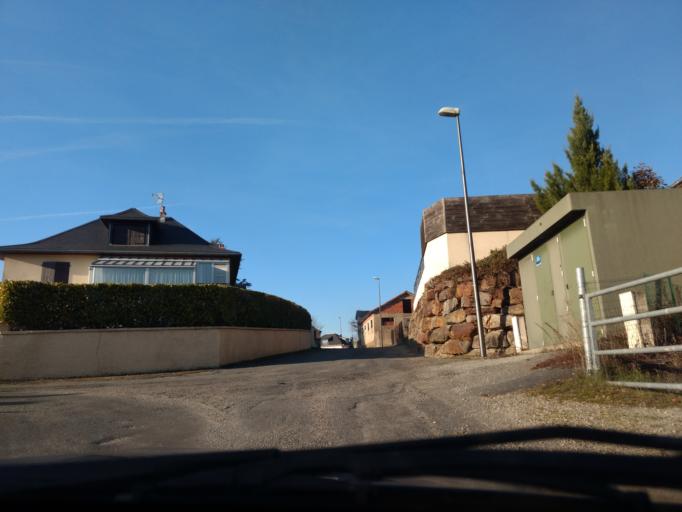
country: FR
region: Midi-Pyrenees
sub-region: Departement de l'Aveyron
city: Naucelle
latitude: 44.1966
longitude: 2.3395
